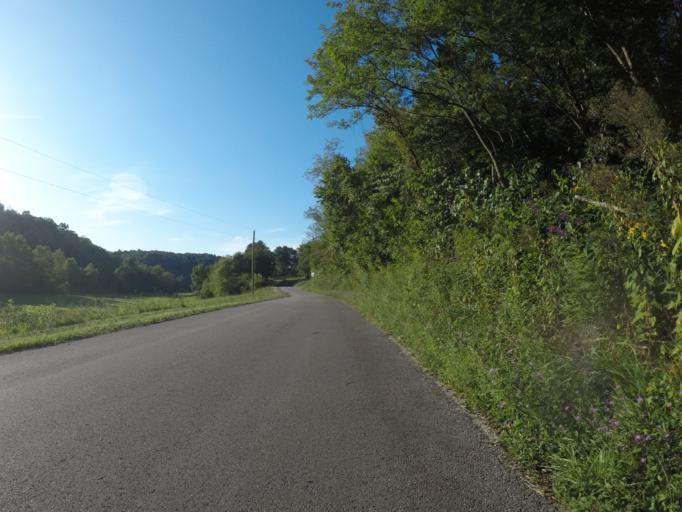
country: US
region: Ohio
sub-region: Lawrence County
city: Coal Grove
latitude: 38.5371
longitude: -82.5461
